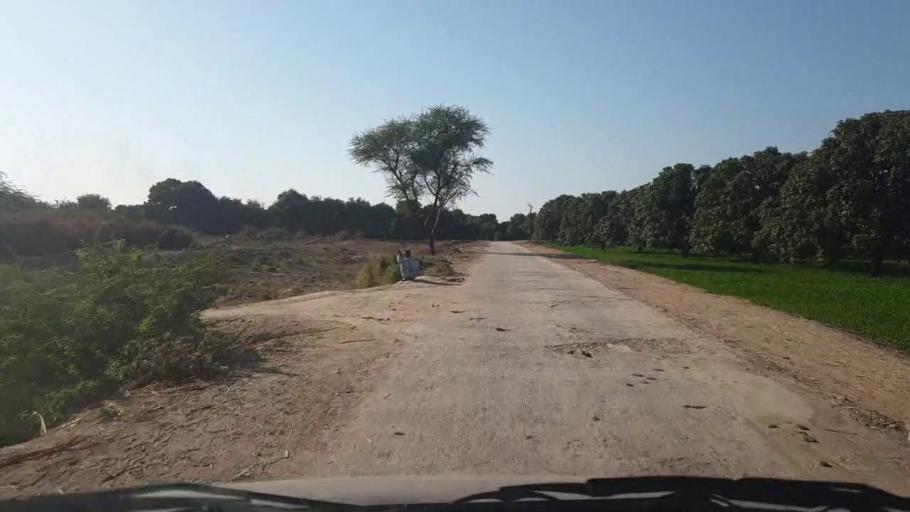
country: PK
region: Sindh
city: Samaro
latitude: 25.3528
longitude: 69.3084
